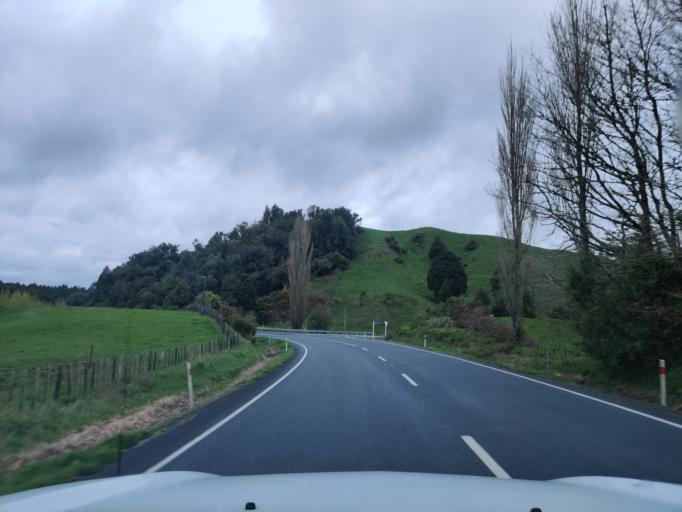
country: NZ
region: Waikato
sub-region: Otorohanga District
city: Otorohanga
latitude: -38.5317
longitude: 175.1777
